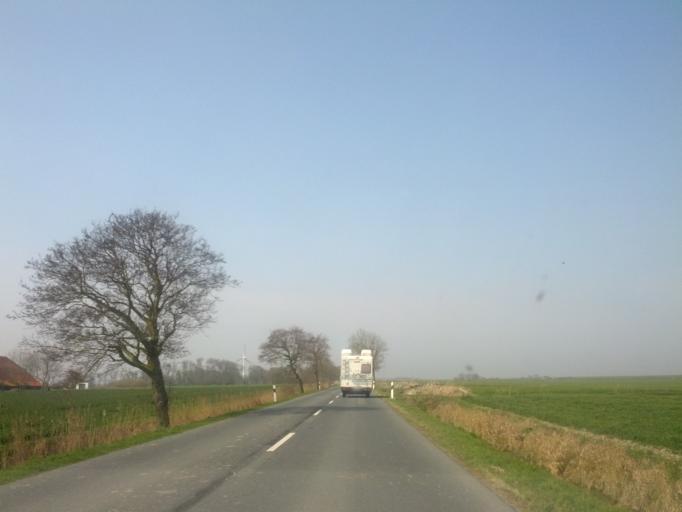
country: DE
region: Lower Saxony
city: Hagermarsch
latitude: 53.6670
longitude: 7.3303
